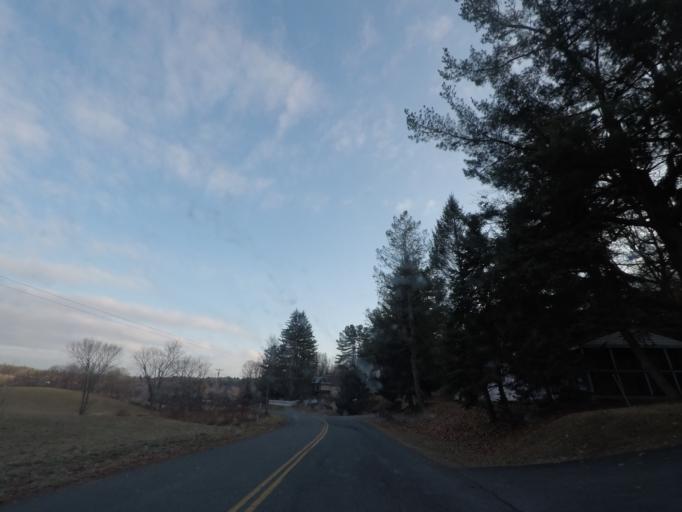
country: US
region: New York
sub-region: Rensselaer County
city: Wynantskill
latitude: 42.7017
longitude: -73.6340
